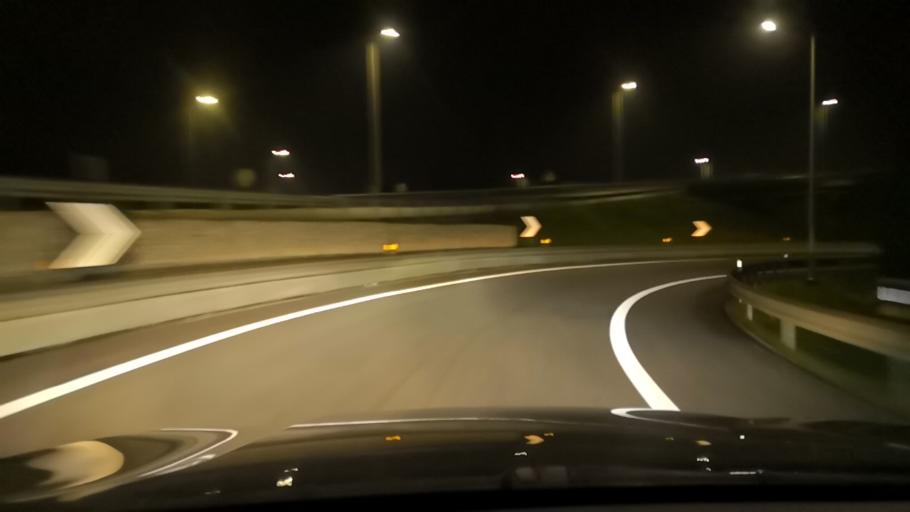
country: PT
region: Setubal
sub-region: Palmela
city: Palmela
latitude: 38.5818
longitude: -8.8646
